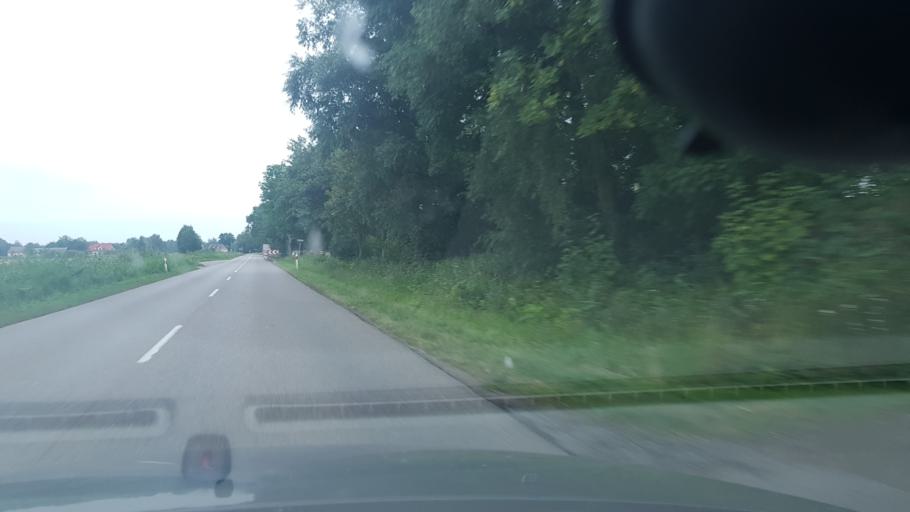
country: PL
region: Pomeranian Voivodeship
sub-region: Powiat nowodworski
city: Nowy Dwor Gdanski
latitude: 54.2406
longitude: 19.1365
